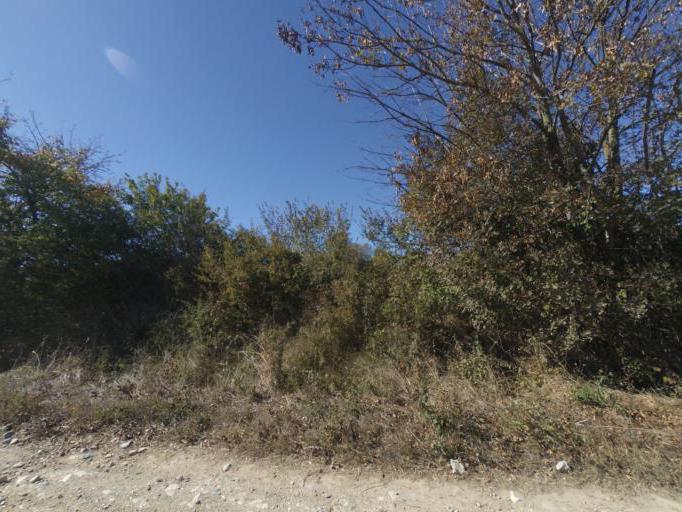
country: FR
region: Languedoc-Roussillon
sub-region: Departement du Gard
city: Vergeze
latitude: 43.7558
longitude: 4.2116
